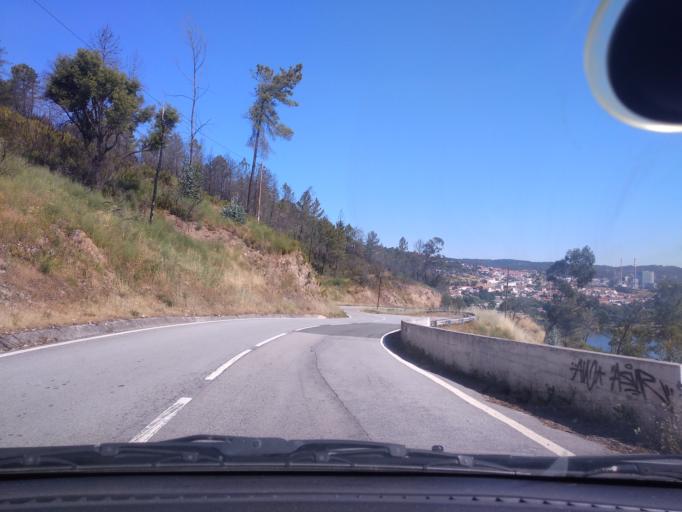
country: PT
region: Portalegre
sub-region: Nisa
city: Nisa
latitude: 39.6429
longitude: -7.6697
